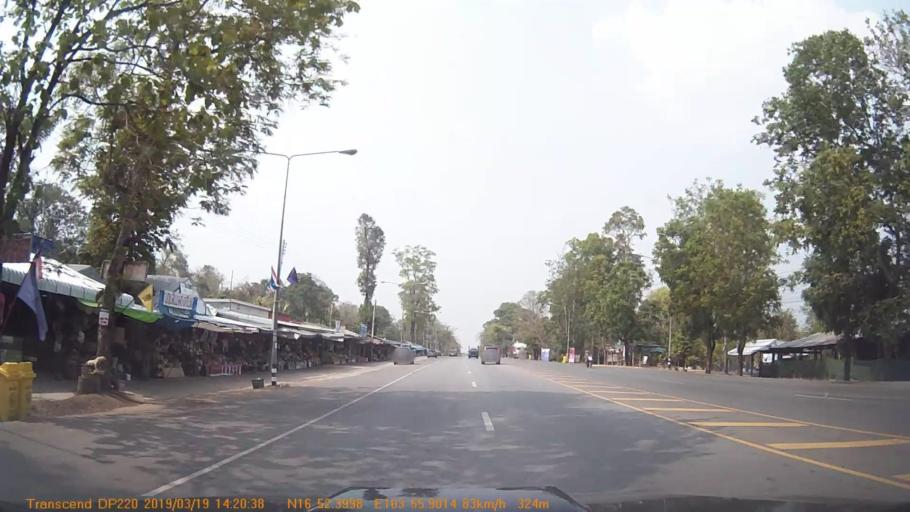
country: TH
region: Sakon Nakhon
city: Phu Phan
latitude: 16.8739
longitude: 103.9316
